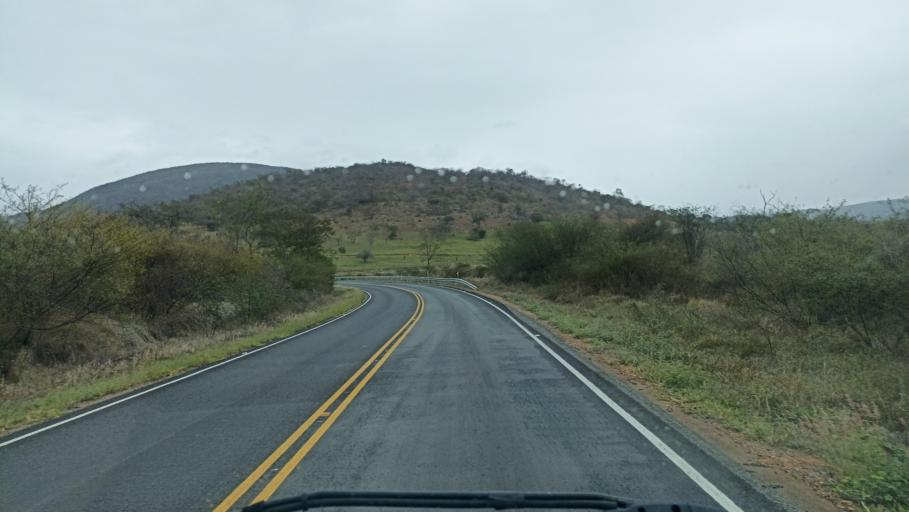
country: BR
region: Bahia
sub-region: Andarai
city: Vera Cruz
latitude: -13.0452
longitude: -40.7719
